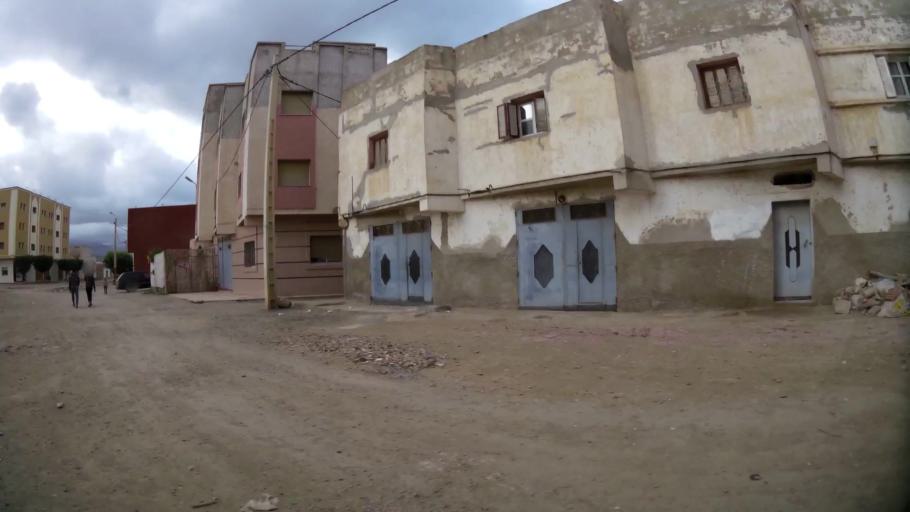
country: MA
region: Oriental
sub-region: Nador
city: Nador
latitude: 35.1573
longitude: -2.9152
